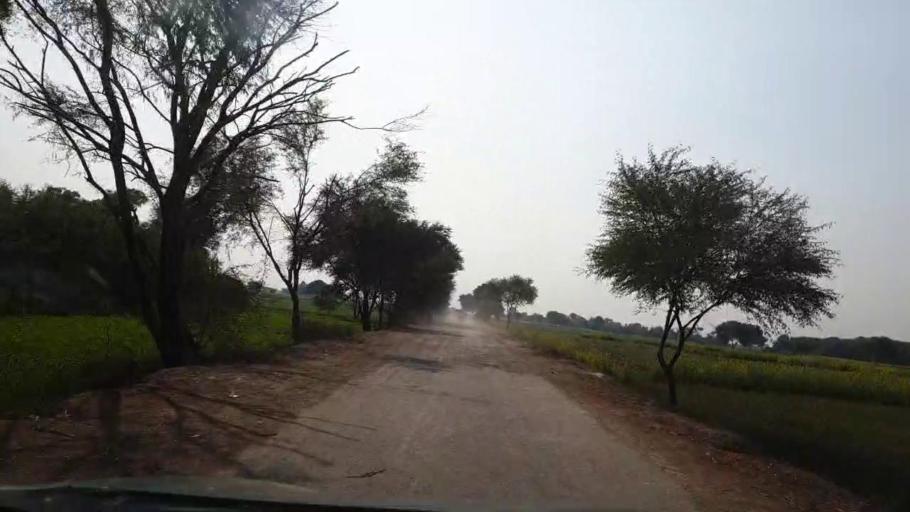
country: PK
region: Sindh
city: Bhit Shah
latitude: 25.7512
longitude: 68.4955
